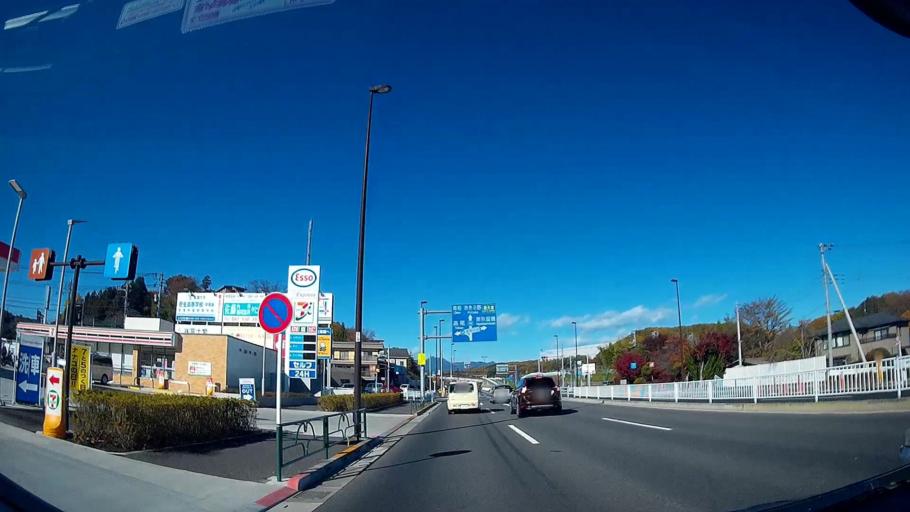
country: JP
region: Tokyo
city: Fussa
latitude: 35.7062
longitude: 139.2973
